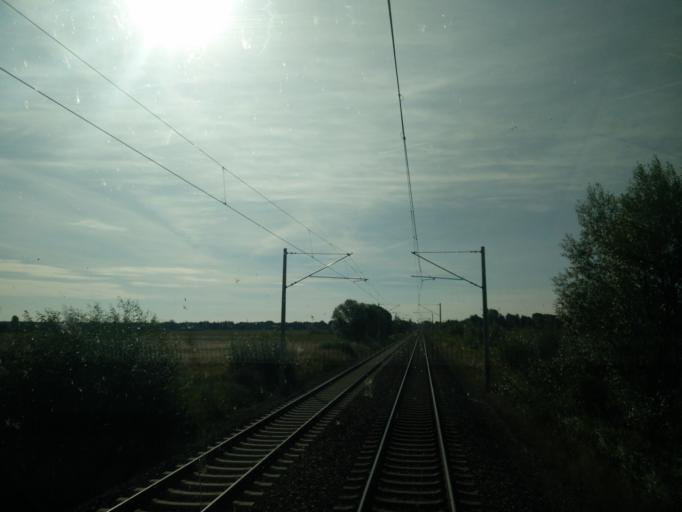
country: DE
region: Brandenburg
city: Luebben
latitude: 51.9682
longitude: 13.8123
